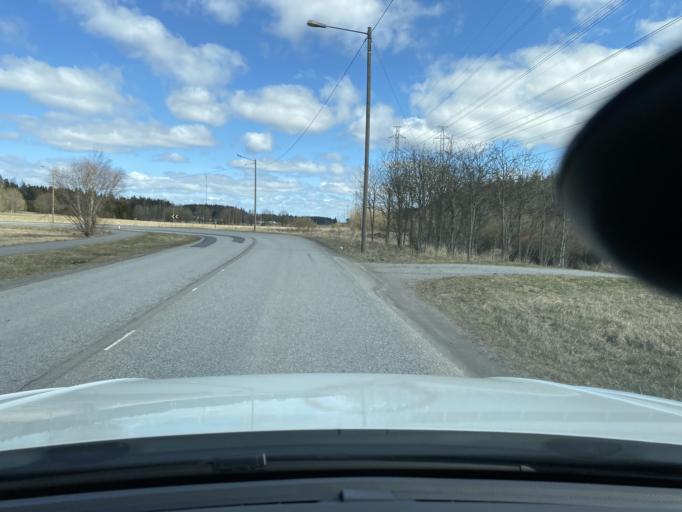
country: FI
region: Varsinais-Suomi
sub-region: Turku
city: Turku
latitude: 60.4742
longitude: 22.3185
